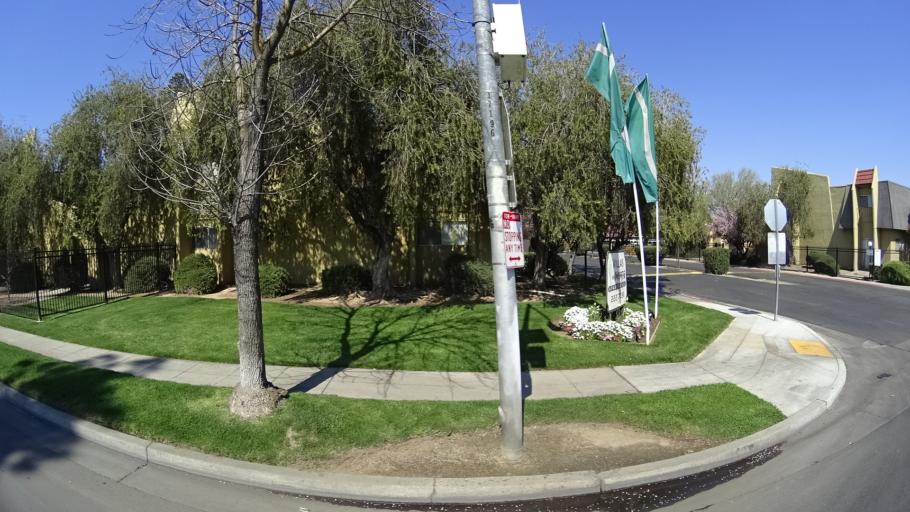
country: US
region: California
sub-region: Fresno County
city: Fresno
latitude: 36.7939
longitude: -119.8333
